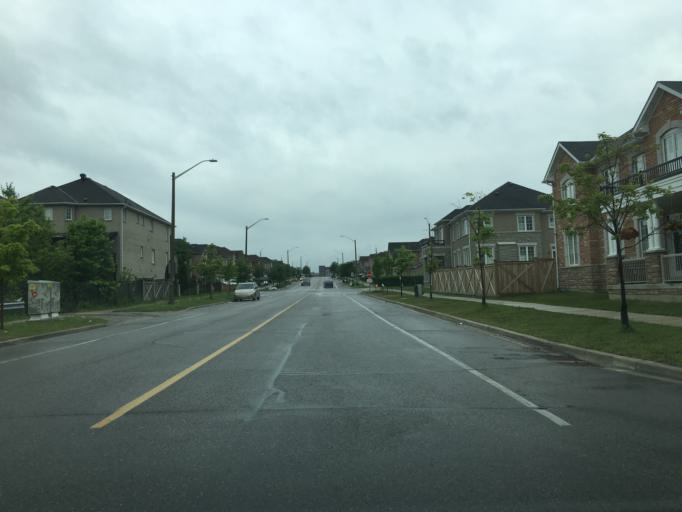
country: CA
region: Ontario
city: Markham
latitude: 43.8414
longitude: -79.2472
